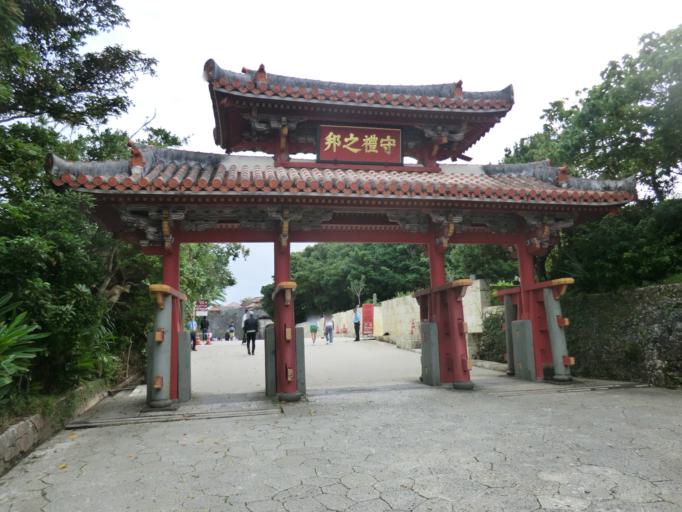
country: JP
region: Okinawa
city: Naha-shi
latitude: 26.2182
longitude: 127.7168
